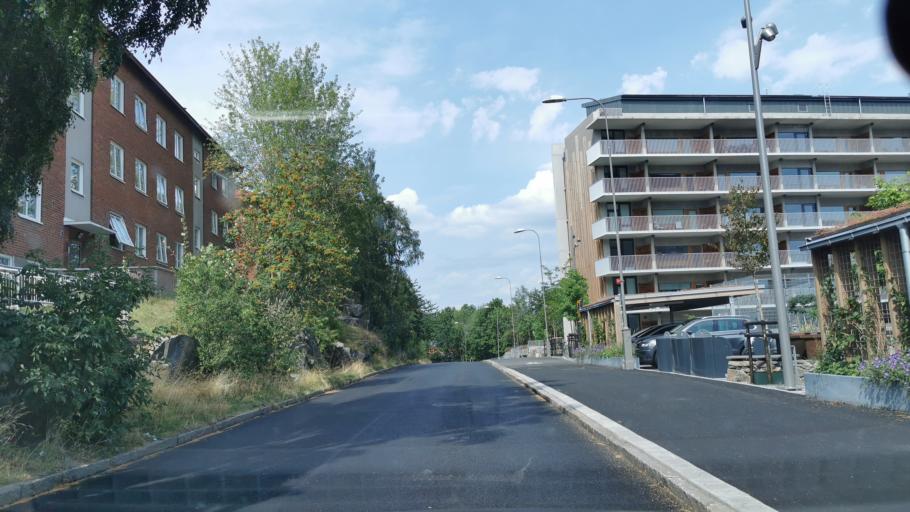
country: SE
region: Vaestra Goetaland
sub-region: Goteborg
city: Goeteborg
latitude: 57.6825
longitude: 11.9785
